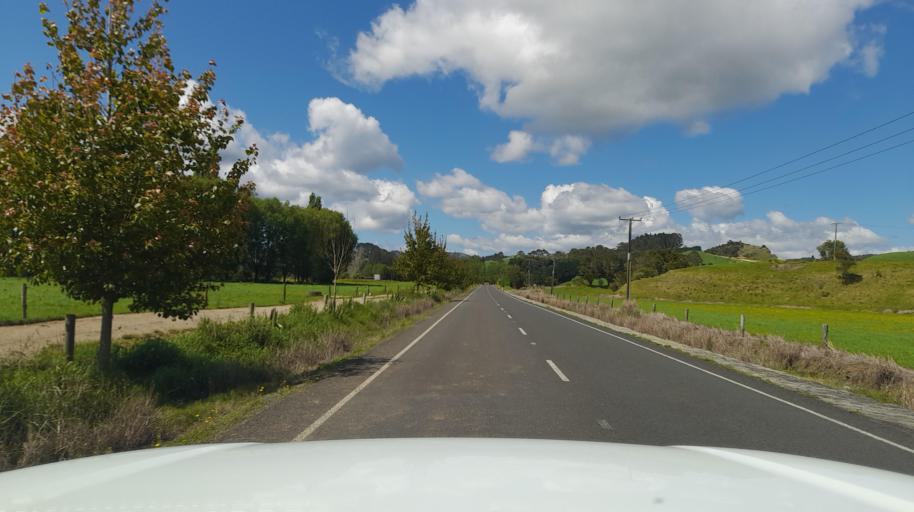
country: NZ
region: Northland
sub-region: Far North District
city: Taipa
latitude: -35.0627
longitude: 173.5025
